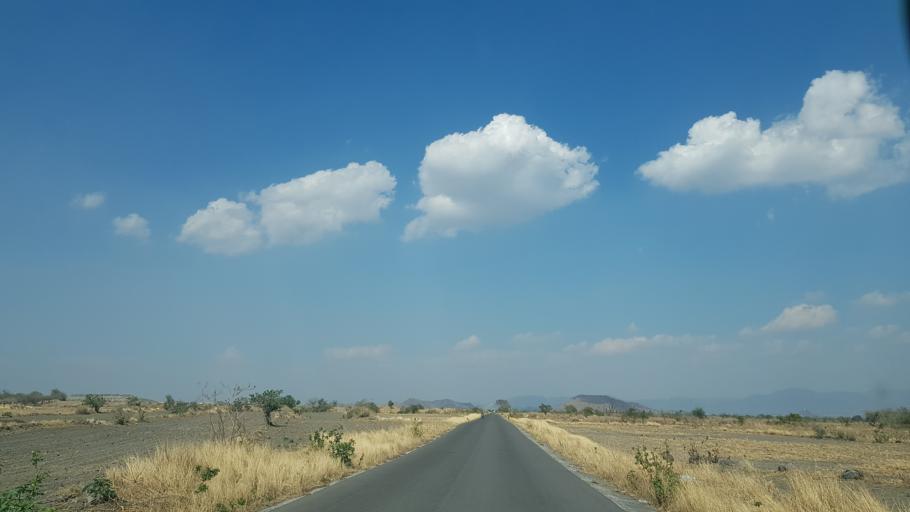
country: MX
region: Puebla
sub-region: Atlixco
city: Colonia Agricola de Ocotepec (Colonia San Jose)
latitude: 18.9189
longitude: -98.5221
